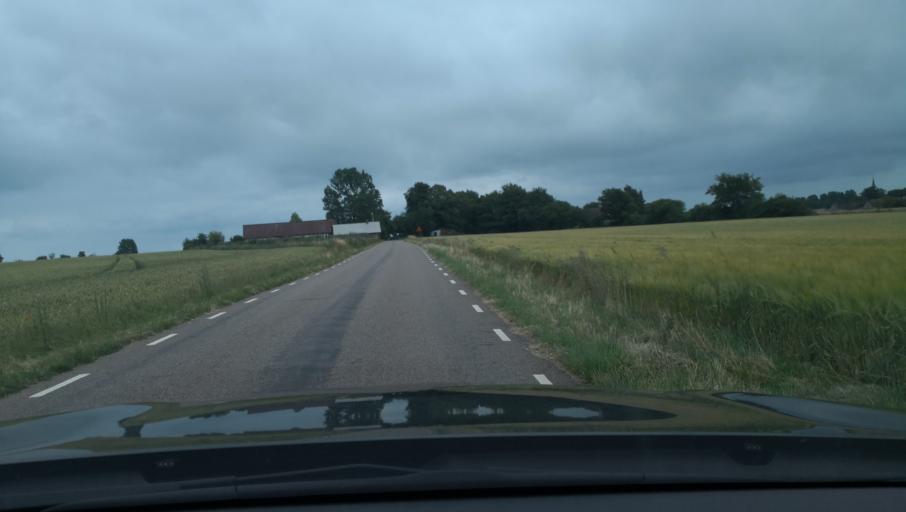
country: SE
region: Skane
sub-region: Simrishamns Kommun
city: Kivik
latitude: 55.6709
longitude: 14.1998
